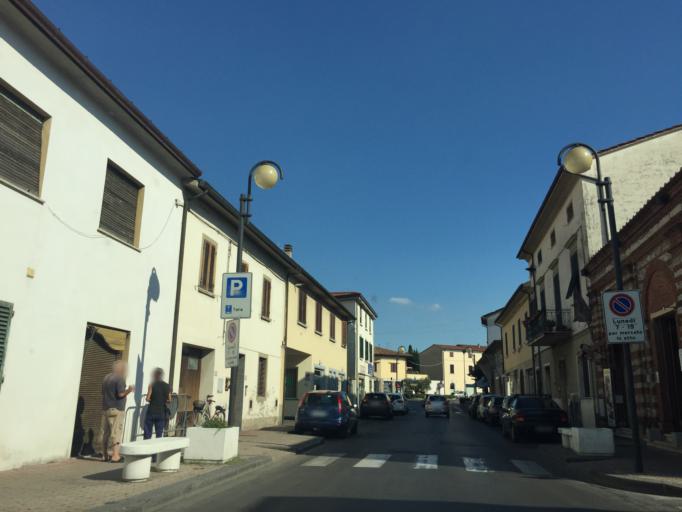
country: IT
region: Tuscany
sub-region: Provincia di Pistoia
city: Monsummano Terme
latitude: 43.8701
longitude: 10.8127
